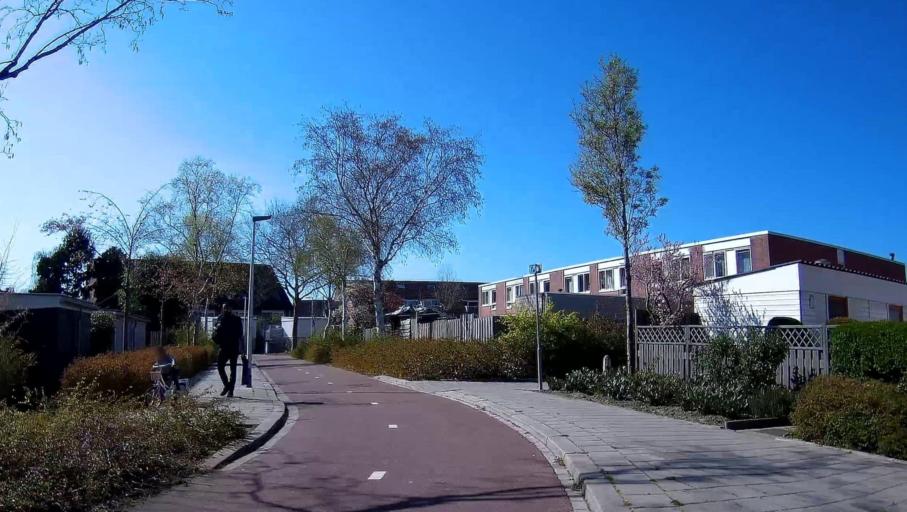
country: NL
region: South Holland
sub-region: Gemeente Capelle aan den IJssel
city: Capelle aan den IJssel
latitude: 51.9480
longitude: 4.5770
